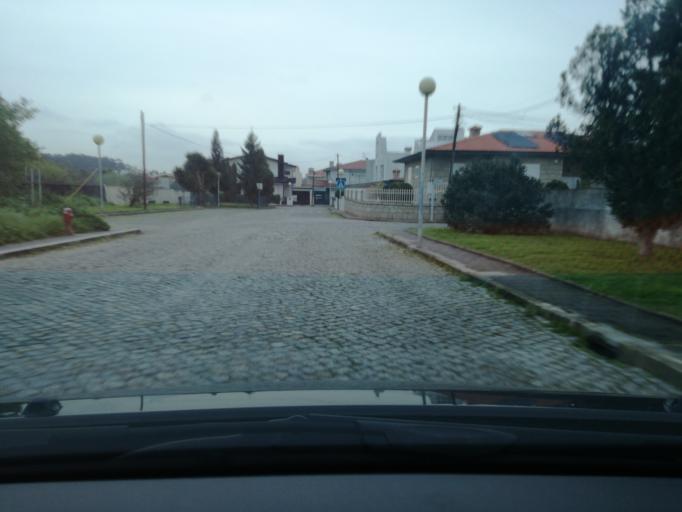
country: PT
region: Porto
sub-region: Maia
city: Gemunde
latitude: 41.2578
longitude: -8.6683
